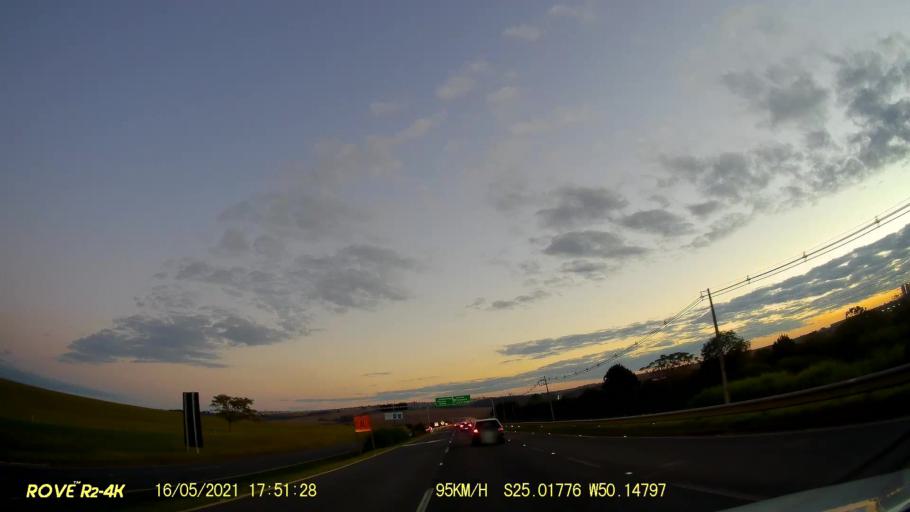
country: BR
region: Parana
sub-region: Carambei
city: Carambei
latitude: -25.0180
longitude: -50.1481
